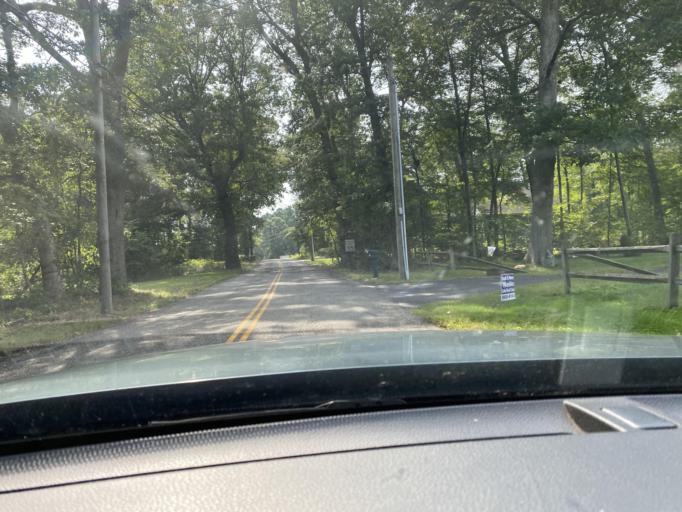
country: US
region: Connecticut
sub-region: New London County
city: Colchester
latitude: 41.6283
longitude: -72.3029
